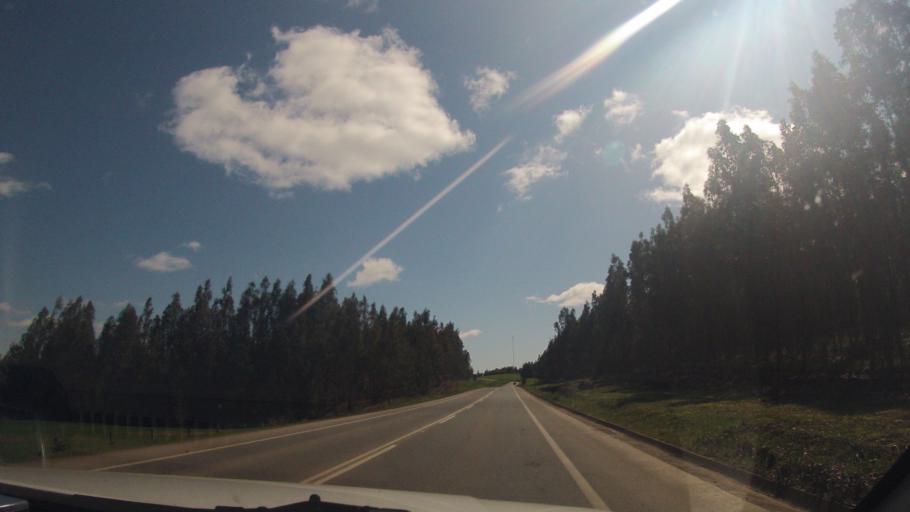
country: CL
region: Araucania
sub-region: Provincia de Malleco
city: Traiguen
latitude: -38.2039
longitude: -72.7491
